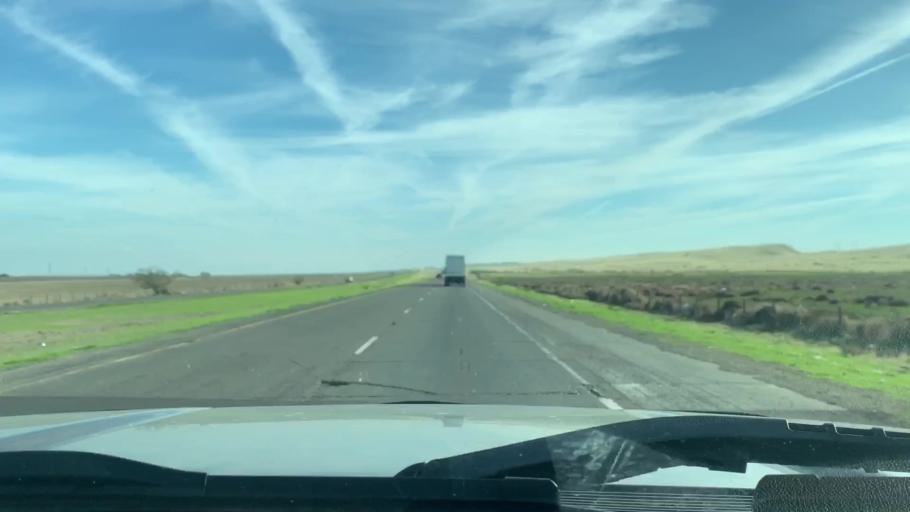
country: US
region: California
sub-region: Fresno County
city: Coalinga
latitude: 36.3519
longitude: -120.3194
